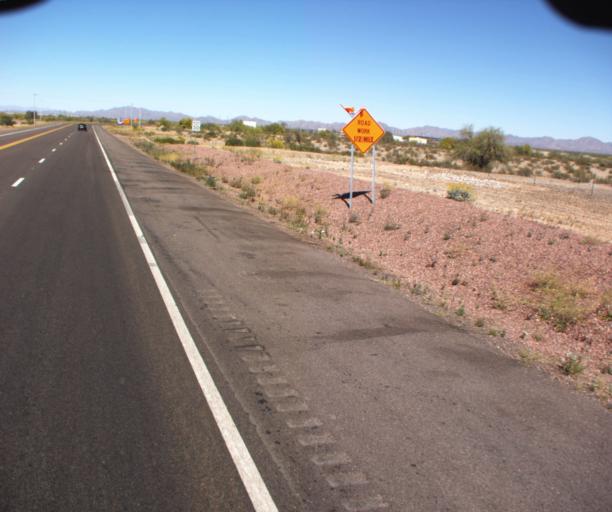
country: US
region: Arizona
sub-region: Maricopa County
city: Gila Bend
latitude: 32.9541
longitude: -112.6851
